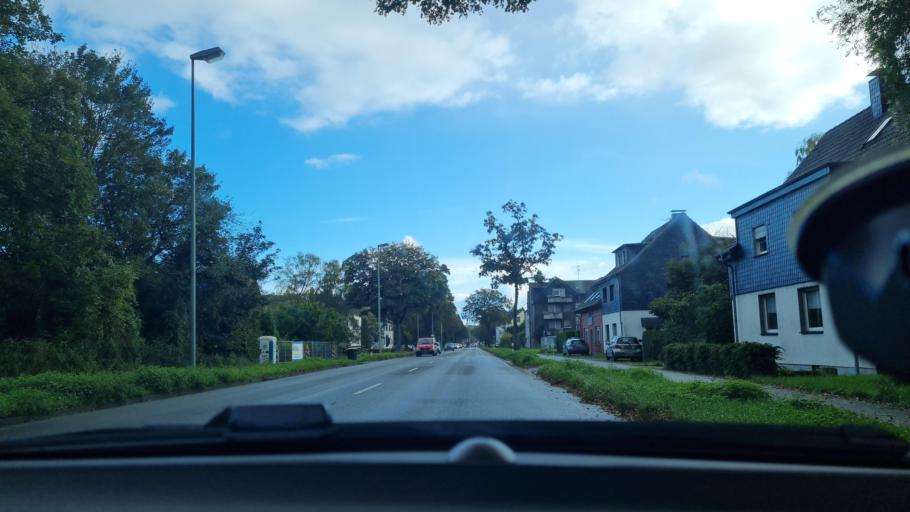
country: DE
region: North Rhine-Westphalia
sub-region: Regierungsbezirk Dusseldorf
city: Dinslaken
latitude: 51.5773
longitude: 6.7275
